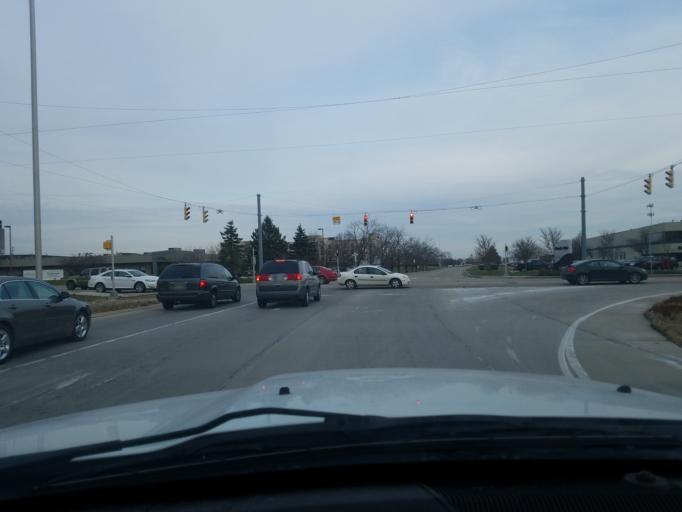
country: US
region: Indiana
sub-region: Boone County
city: Zionsville
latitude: 39.8848
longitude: -86.2673
